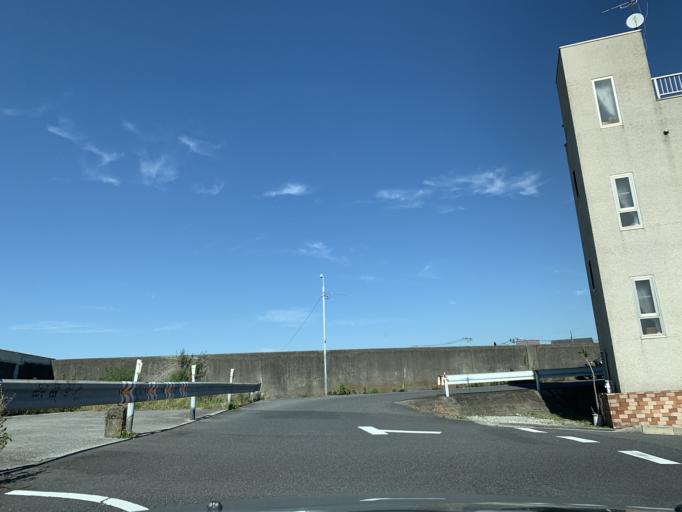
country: JP
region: Tokyo
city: Urayasu
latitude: 35.6556
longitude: 139.8888
